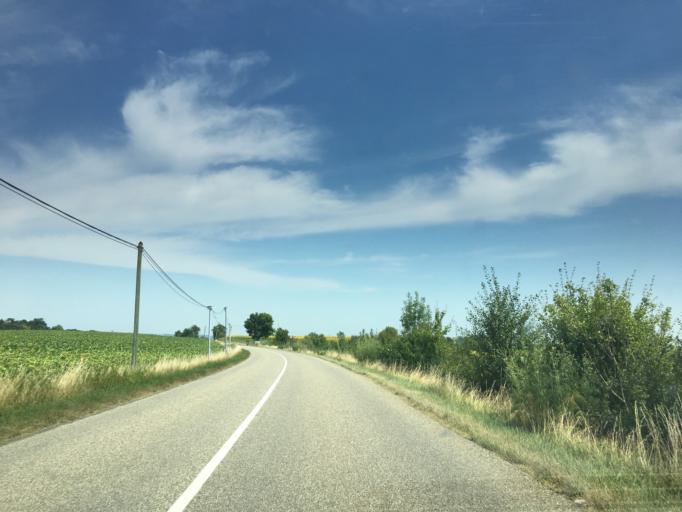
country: FR
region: Midi-Pyrenees
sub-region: Departement du Gers
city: Fleurance
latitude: 43.8628
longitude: 0.7229
